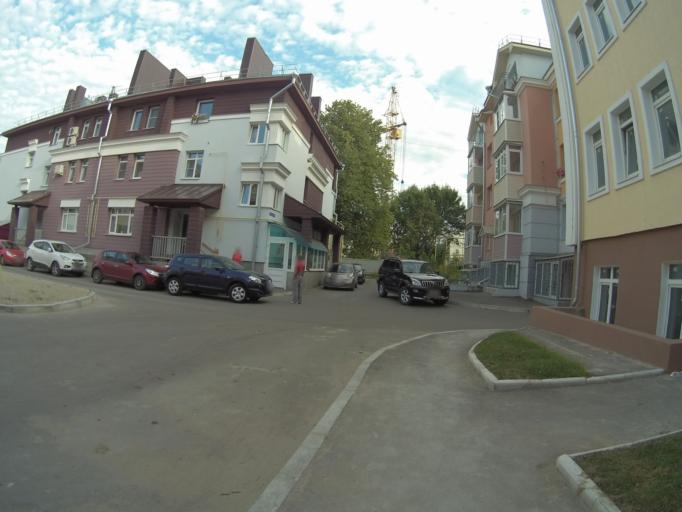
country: RU
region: Vladimir
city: Vladimir
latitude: 56.1368
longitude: 40.4258
